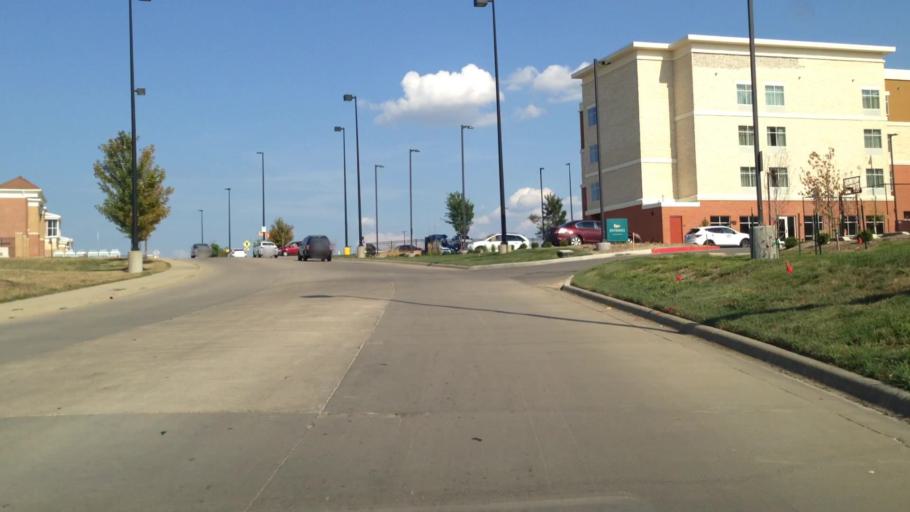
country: US
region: Kansas
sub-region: Wyandotte County
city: Edwardsville
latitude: 39.1306
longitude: -94.8326
